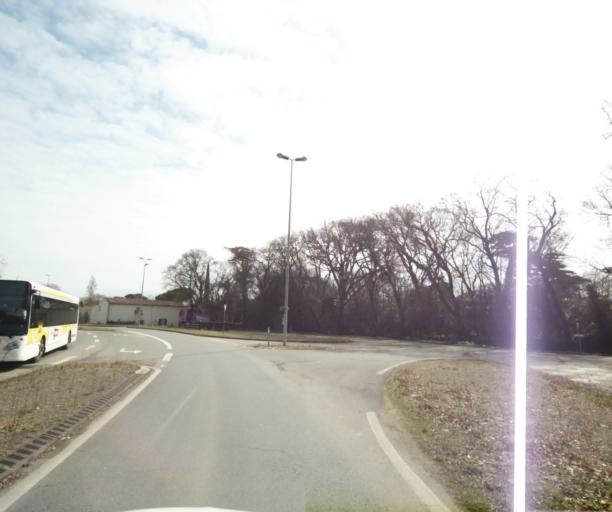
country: FR
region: Poitou-Charentes
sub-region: Departement de la Charente-Maritime
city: Lagord
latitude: 46.1823
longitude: -1.1734
